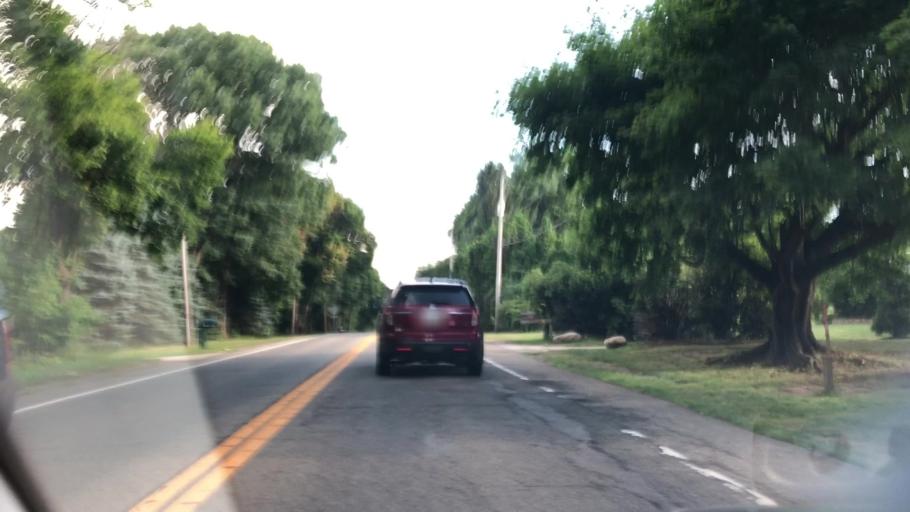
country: US
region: Ohio
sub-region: Summit County
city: Green
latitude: 40.9590
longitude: -81.4941
